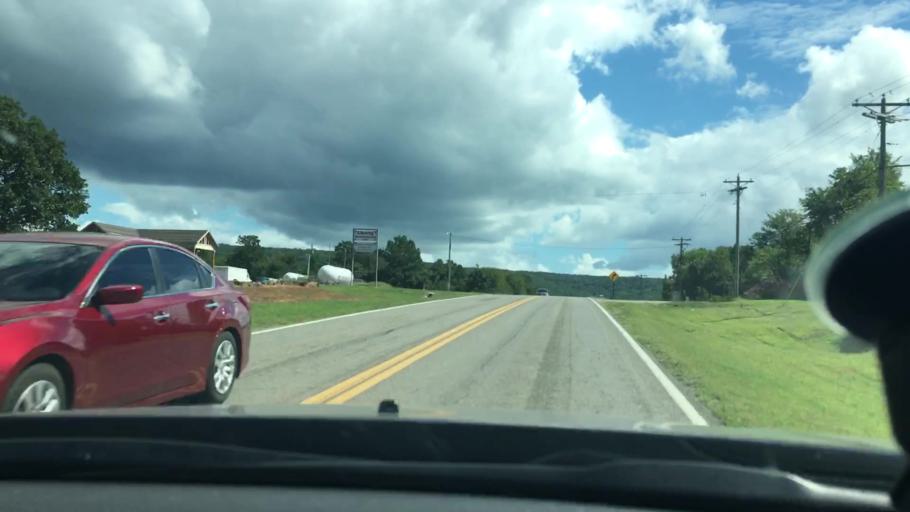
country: US
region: Oklahoma
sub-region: Cherokee County
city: Park Hill
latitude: 35.6916
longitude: -94.9126
